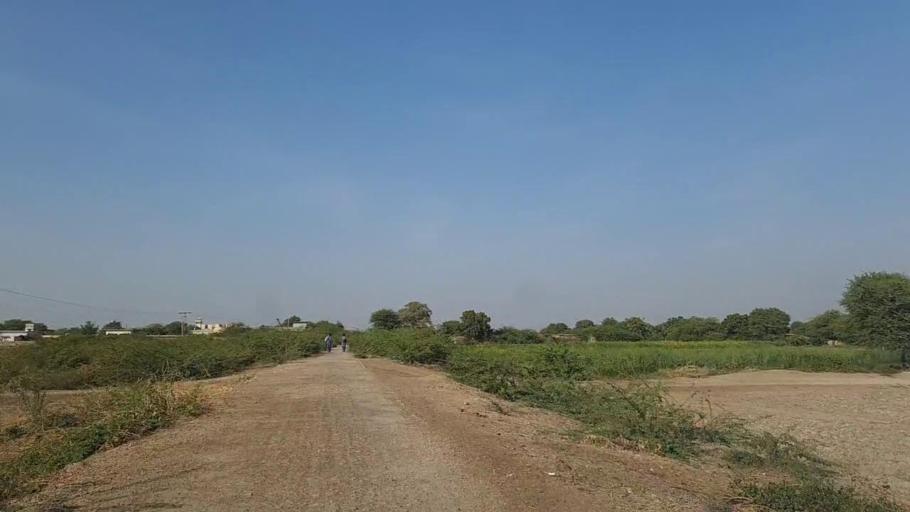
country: PK
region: Sindh
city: Naukot
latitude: 24.9337
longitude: 69.4590
